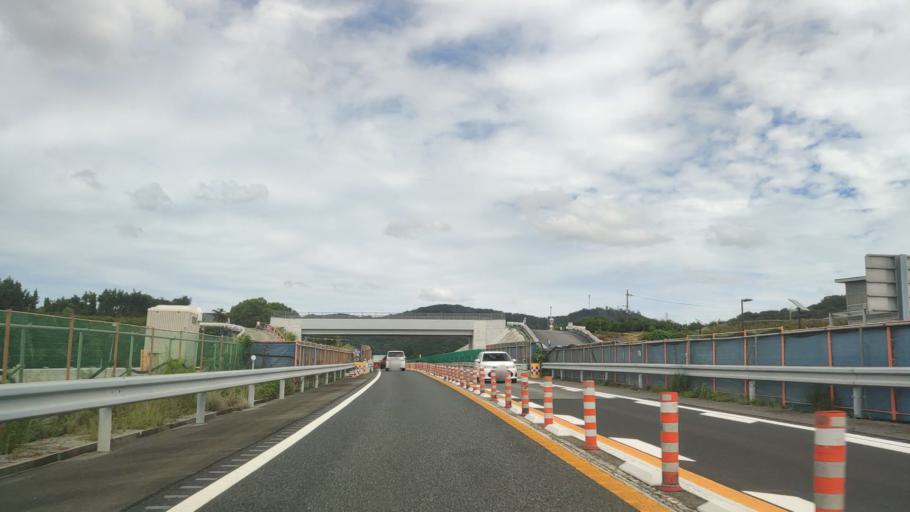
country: JP
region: Wakayama
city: Gobo
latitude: 33.9082
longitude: 135.1938
